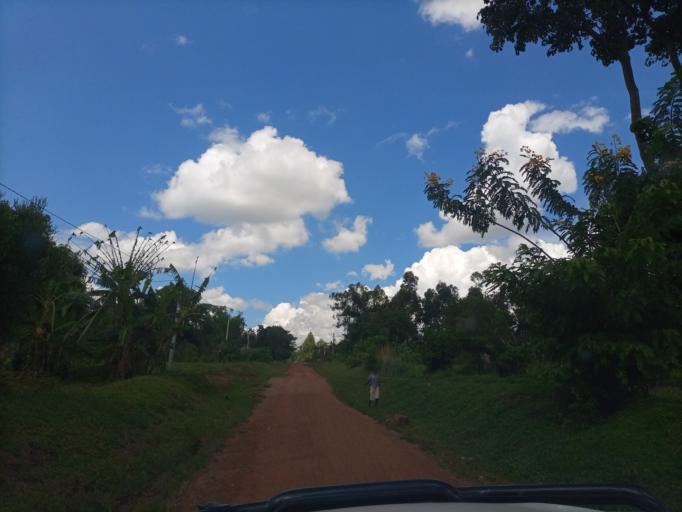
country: UG
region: Eastern Region
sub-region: Tororo District
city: Tororo
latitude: 0.7053
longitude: 34.0137
